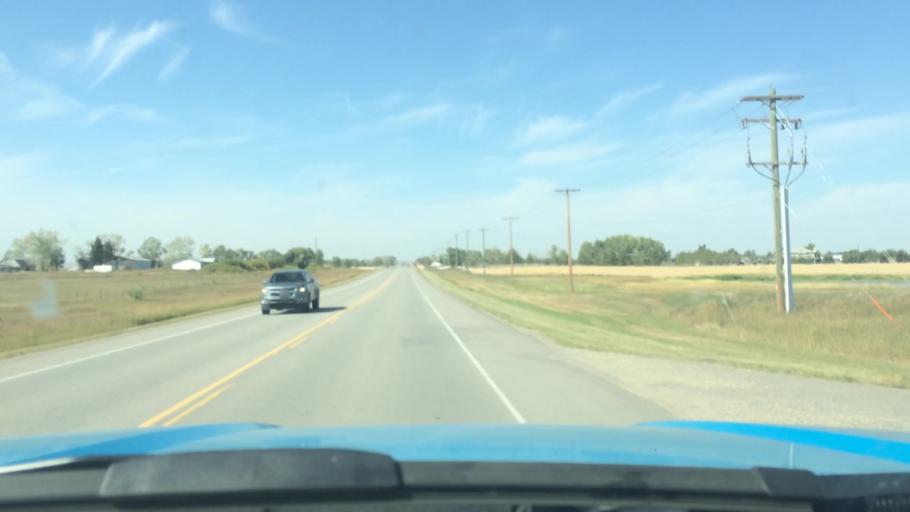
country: CA
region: Alberta
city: Airdrie
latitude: 51.2126
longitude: -113.9419
